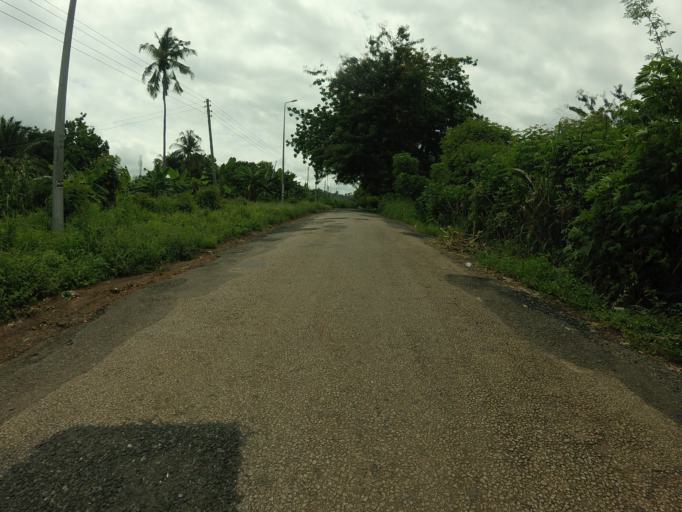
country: GH
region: Volta
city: Ho
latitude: 6.6053
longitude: 0.4618
